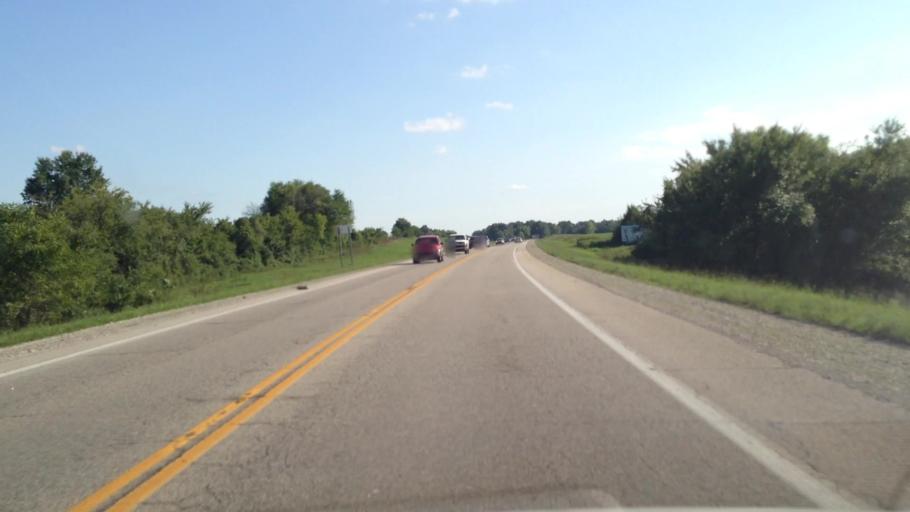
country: US
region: Kansas
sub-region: Crawford County
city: Arma
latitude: 37.5361
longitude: -94.7098
